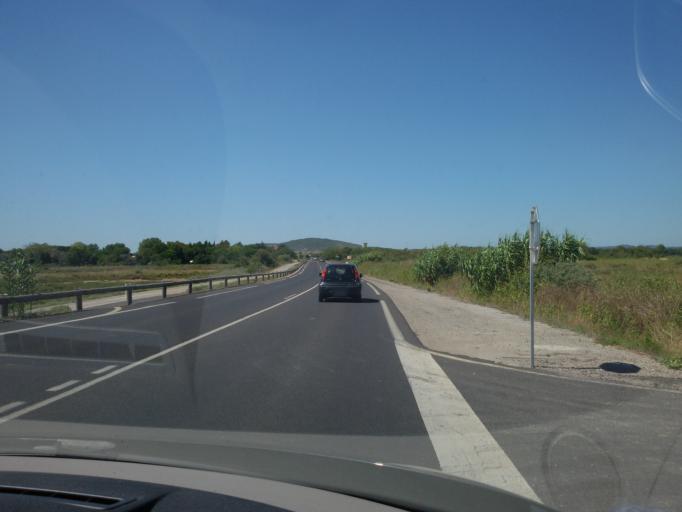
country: FR
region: Languedoc-Roussillon
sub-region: Departement de l'Herault
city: Villeneuve-les-Maguelone
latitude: 43.5389
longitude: 3.8775
